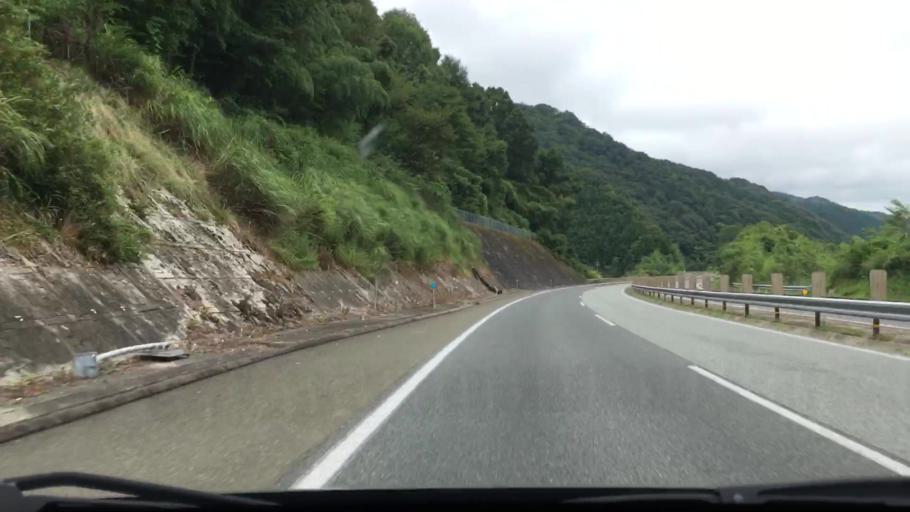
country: JP
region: Hiroshima
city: Shobara
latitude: 34.8382
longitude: 133.0824
